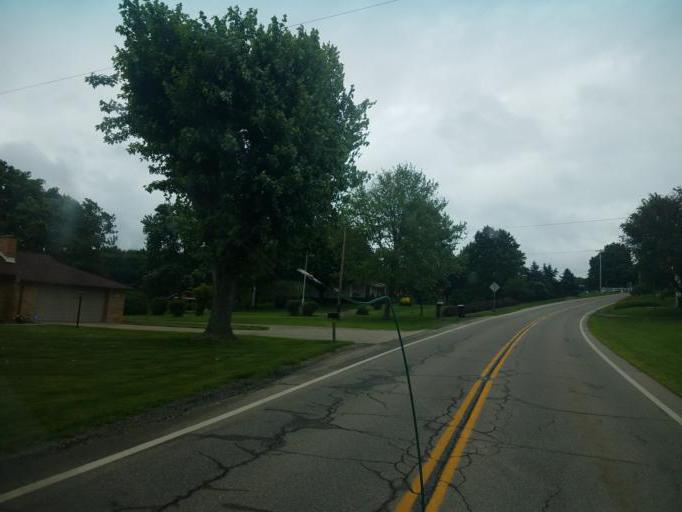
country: US
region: Ohio
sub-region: Carroll County
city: Carrollton
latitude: 40.5988
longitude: -81.0760
